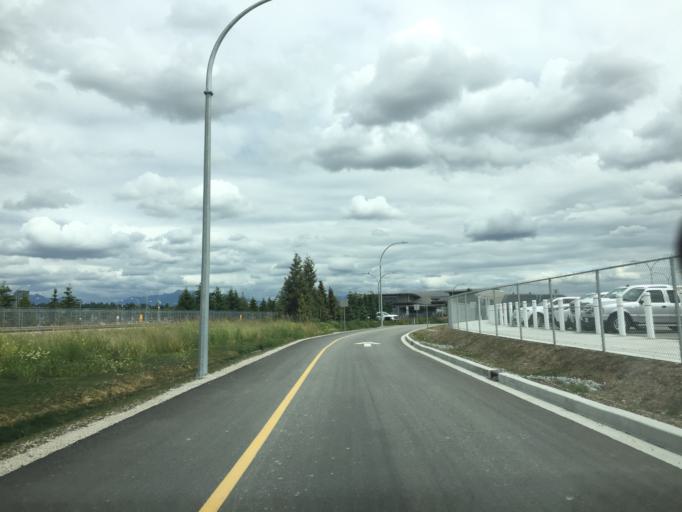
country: CA
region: British Columbia
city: Richmond
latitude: 49.1955
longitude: -123.1490
